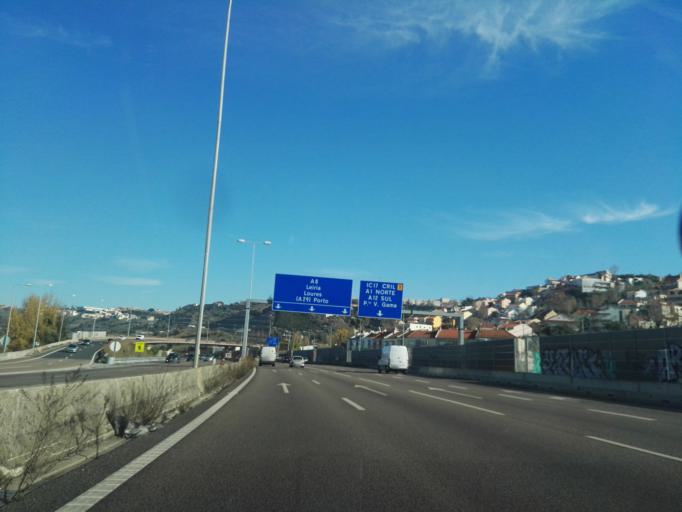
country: PT
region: Lisbon
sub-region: Odivelas
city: Olival do Basto
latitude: 38.7952
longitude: -9.1614
